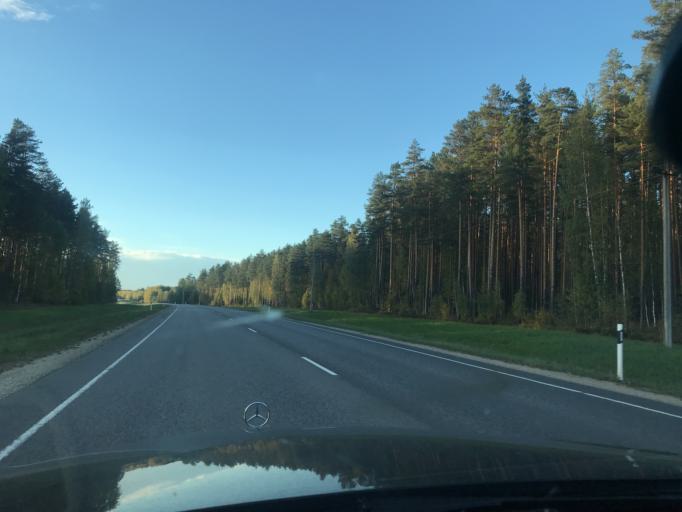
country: EE
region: Vorumaa
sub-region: Voru linn
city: Voru
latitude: 57.8382
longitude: 27.0566
